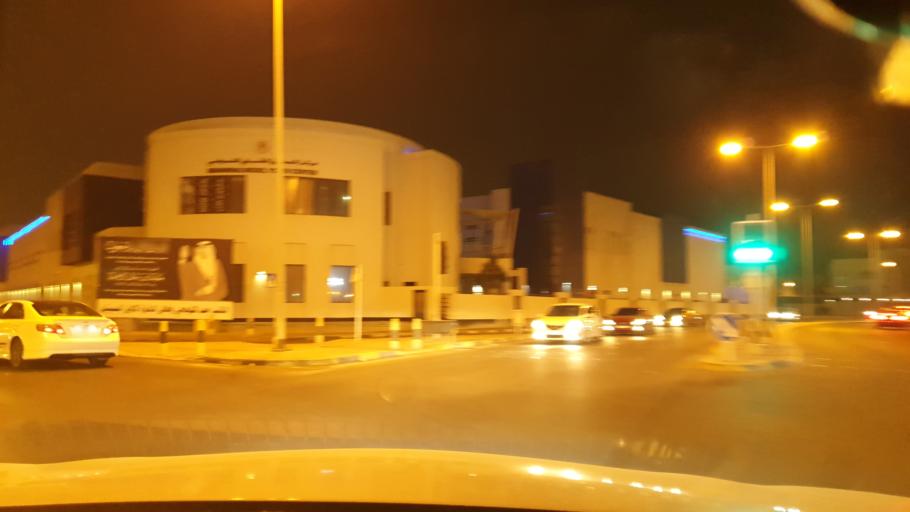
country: BH
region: Muharraq
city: Al Muharraq
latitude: 26.2717
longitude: 50.6042
